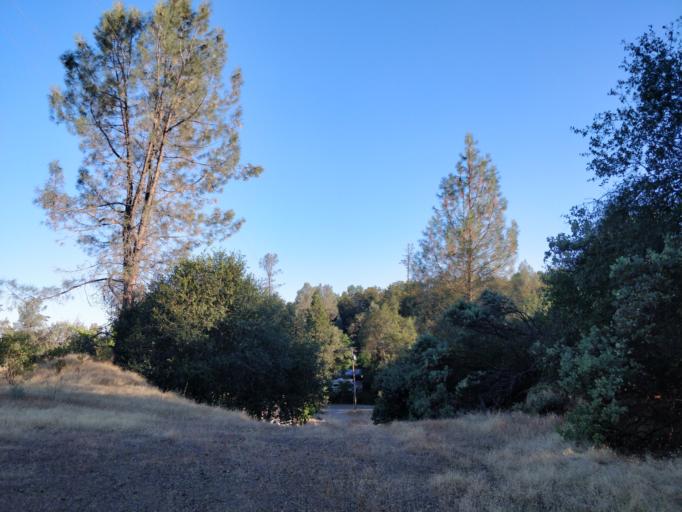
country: US
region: California
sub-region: Shasta County
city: Shasta Lake
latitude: 40.6679
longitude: -122.3615
